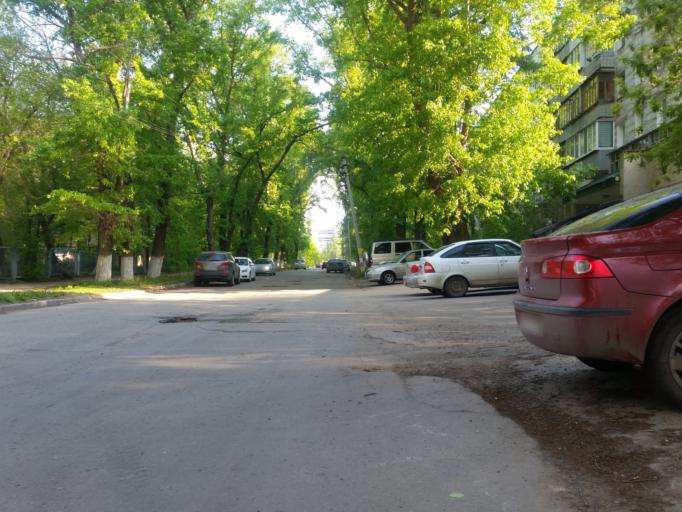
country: RU
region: Ulyanovsk
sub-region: Ulyanovskiy Rayon
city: Ulyanovsk
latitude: 54.3084
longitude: 48.3942
